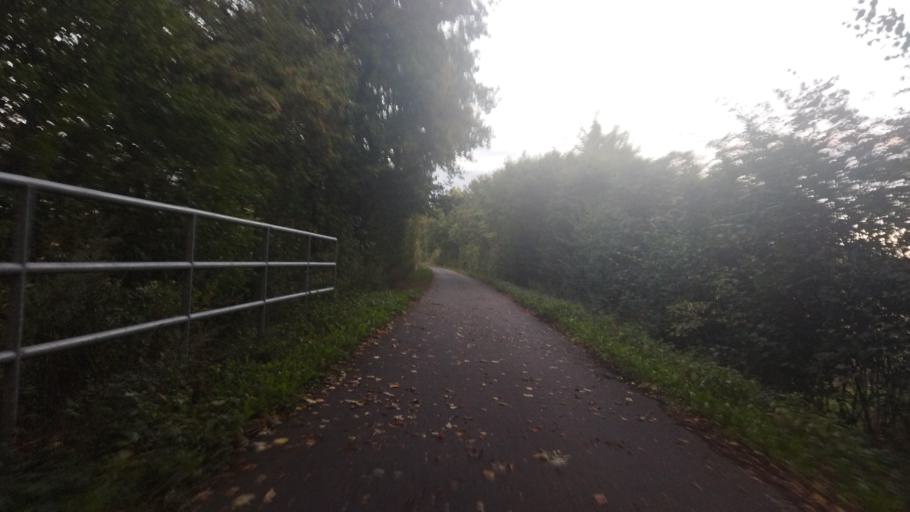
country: DE
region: North Rhine-Westphalia
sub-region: Regierungsbezirk Munster
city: Horstmar
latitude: 52.0316
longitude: 7.3020
